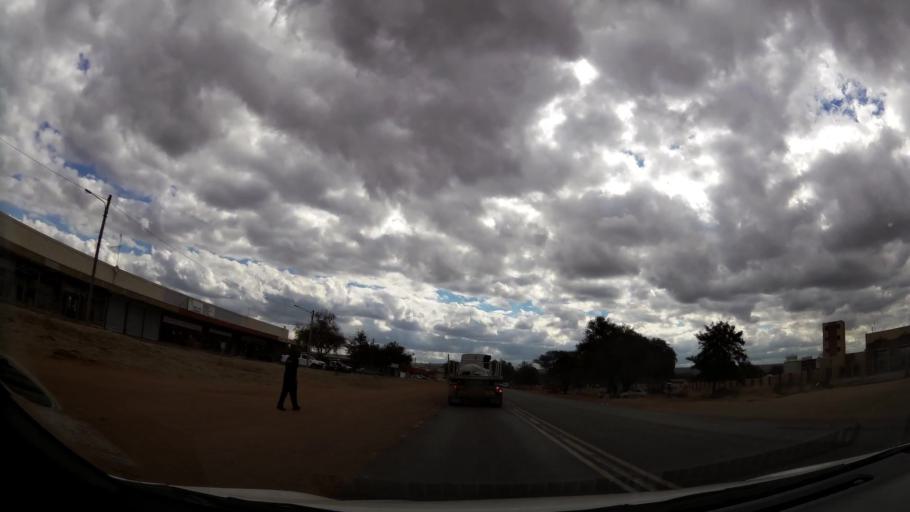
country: ZA
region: Limpopo
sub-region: Waterberg District Municipality
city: Modimolle
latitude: -24.7178
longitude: 28.4214
